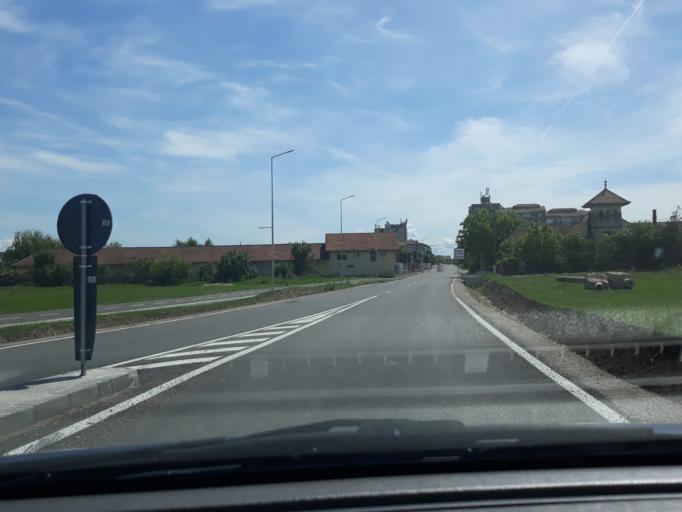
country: RO
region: Bihor
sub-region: Comuna Biharea
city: Oradea
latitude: 47.0703
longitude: 21.8982
